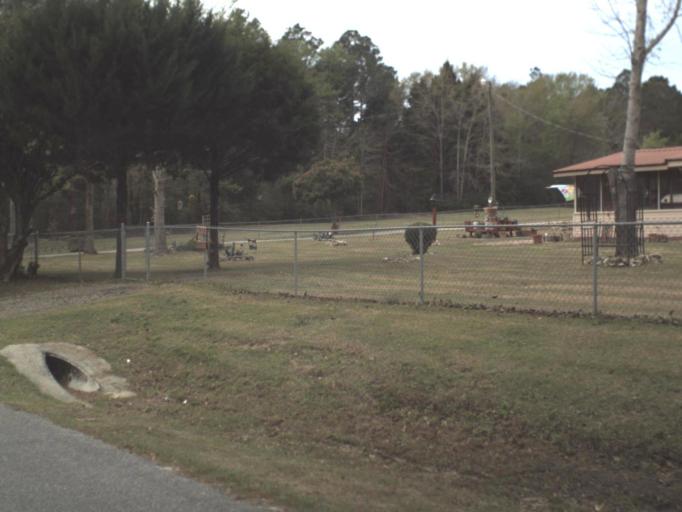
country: US
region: Florida
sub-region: Holmes County
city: Bonifay
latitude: 30.8494
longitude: -85.6667
